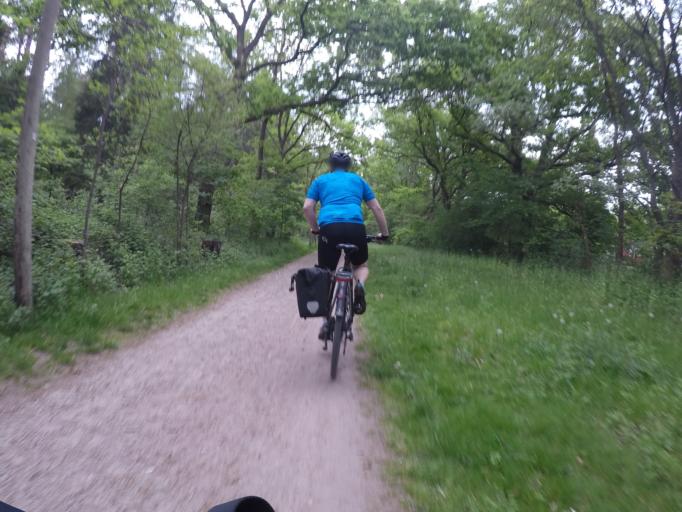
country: DE
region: Schleswig-Holstein
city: Norderstedt
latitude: 53.7128
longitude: 9.9769
